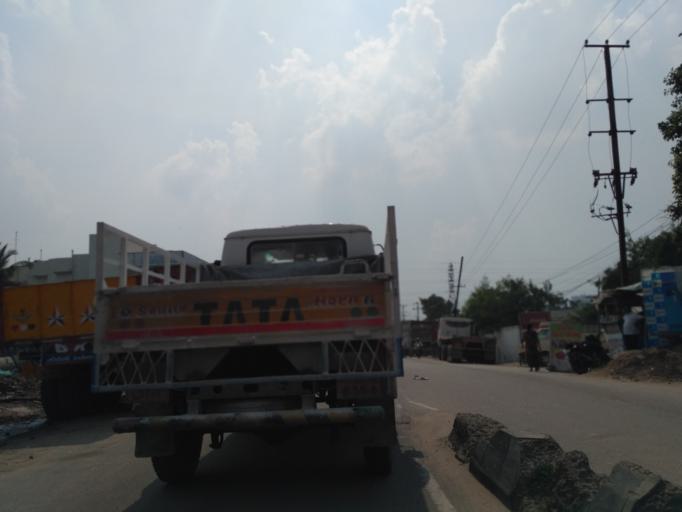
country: IN
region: Telangana
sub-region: Rangareddi
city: Kukatpalli
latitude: 17.4661
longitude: 78.4232
